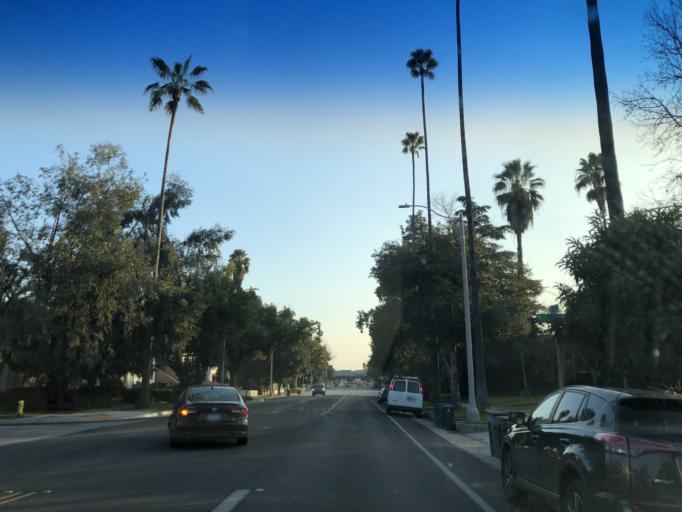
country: US
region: California
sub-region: Los Angeles County
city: Pasadena
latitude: 34.1557
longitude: -118.1215
